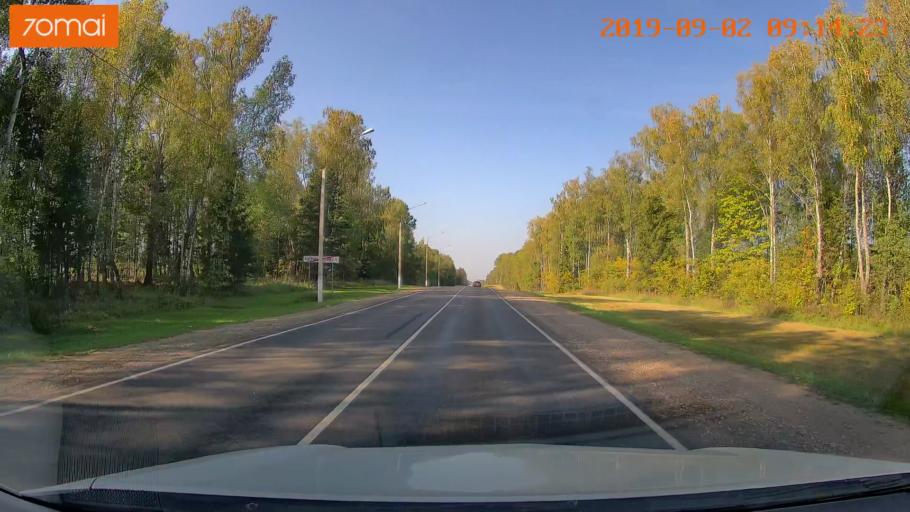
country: RU
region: Kaluga
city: Nikola-Lenivets
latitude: 54.8469
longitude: 35.5165
